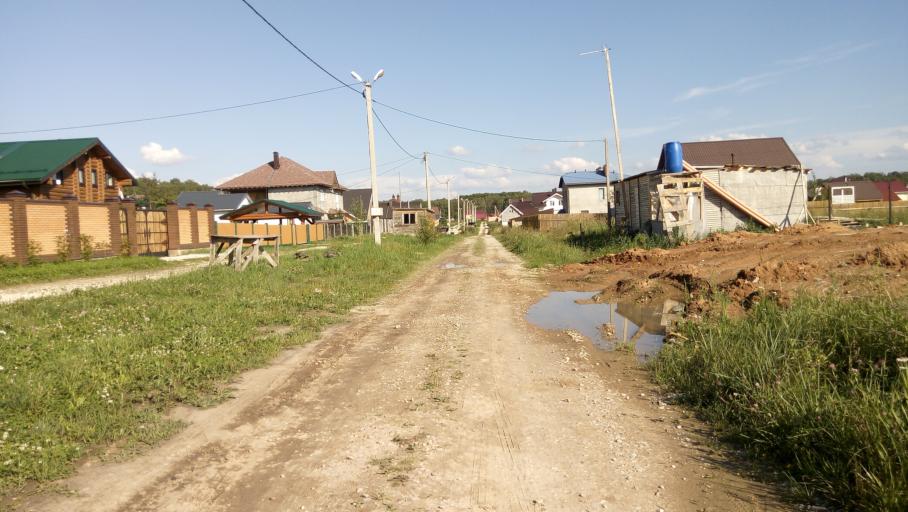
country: RU
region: Moskovskaya
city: Proletarskiy
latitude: 55.0472
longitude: 37.4121
